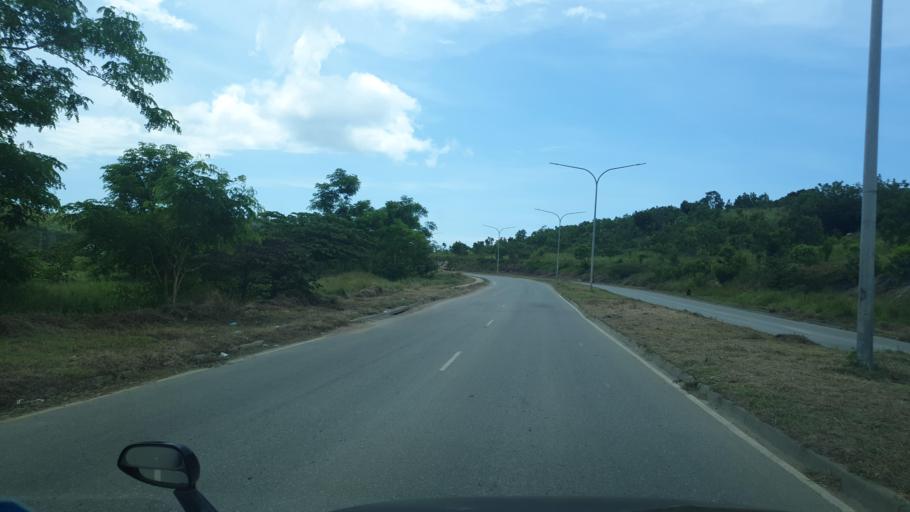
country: PG
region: National Capital
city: Port Moresby
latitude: -9.4272
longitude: 147.1409
